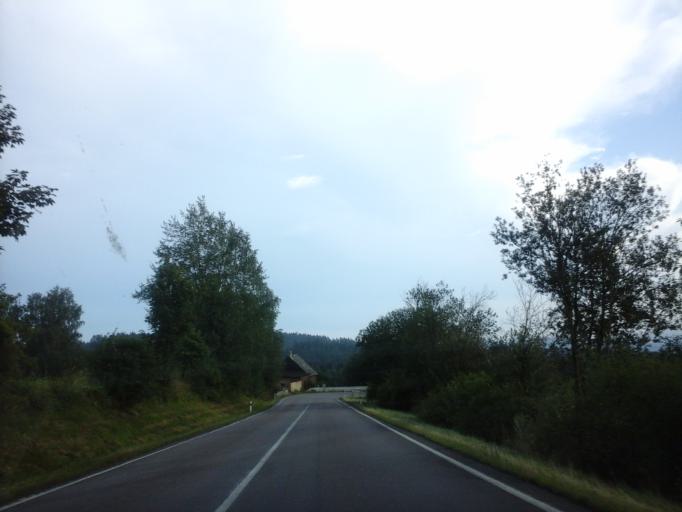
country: CZ
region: Pardubicky
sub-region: Okres Usti nad Orlici
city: Lanskroun
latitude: 49.9326
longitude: 16.6658
